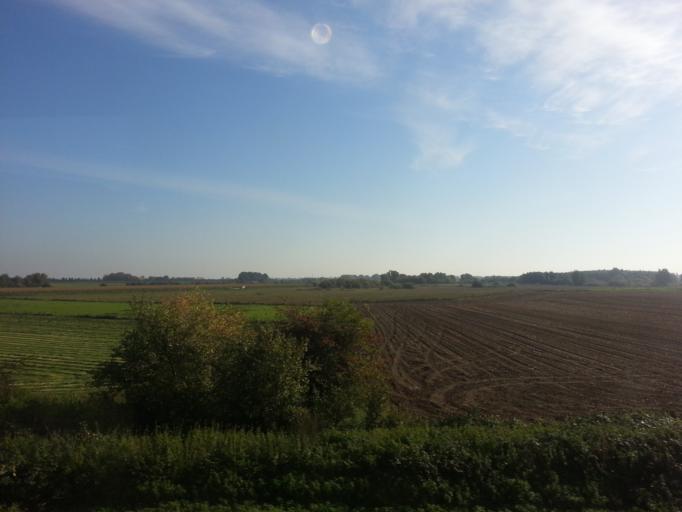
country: NL
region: Gelderland
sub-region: Gemeente Maasdriel
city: Hedel
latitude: 51.7453
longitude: 5.2737
